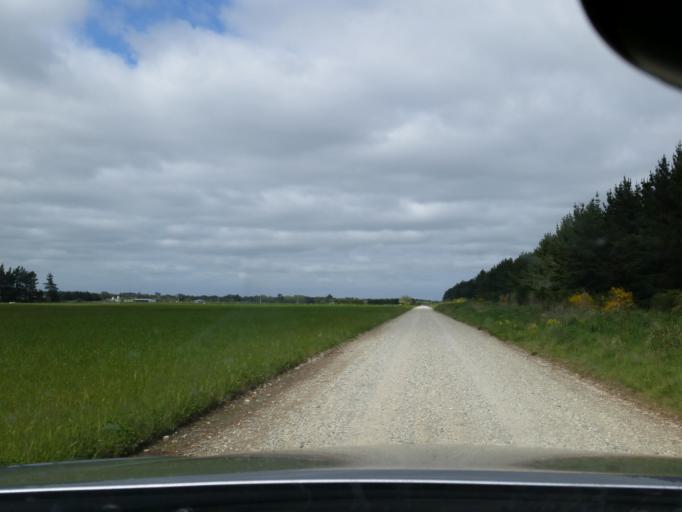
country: NZ
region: Southland
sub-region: Southland District
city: Winton
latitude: -46.2299
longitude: 168.4870
